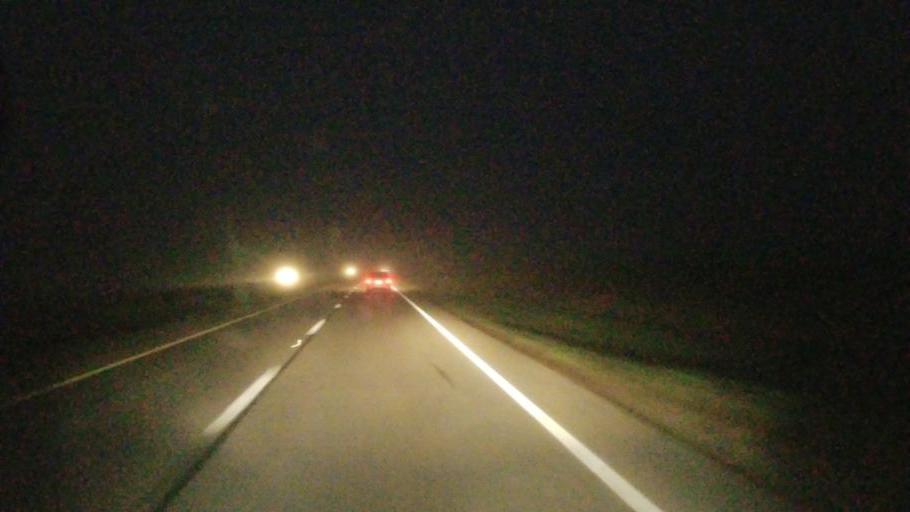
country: US
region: Ohio
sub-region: Pickaway County
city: Logan Elm Village
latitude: 39.5284
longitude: -82.9677
